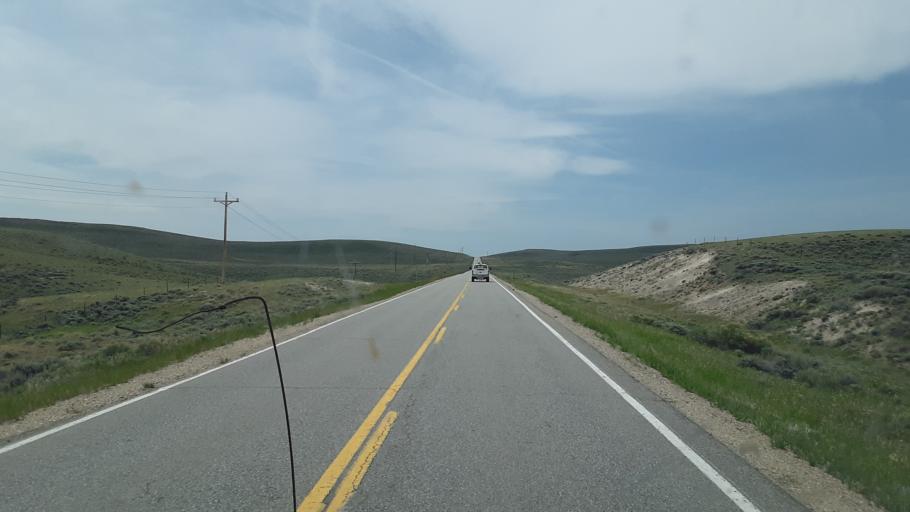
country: US
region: Colorado
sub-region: Jackson County
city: Walden
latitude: 40.6703
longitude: -106.3839
